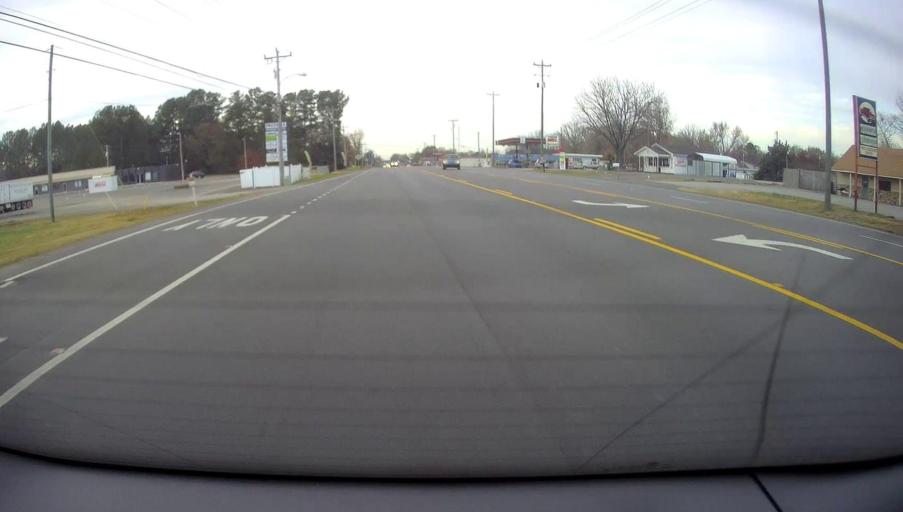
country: US
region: Alabama
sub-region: Morgan County
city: Priceville
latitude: 34.5190
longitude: -86.8867
